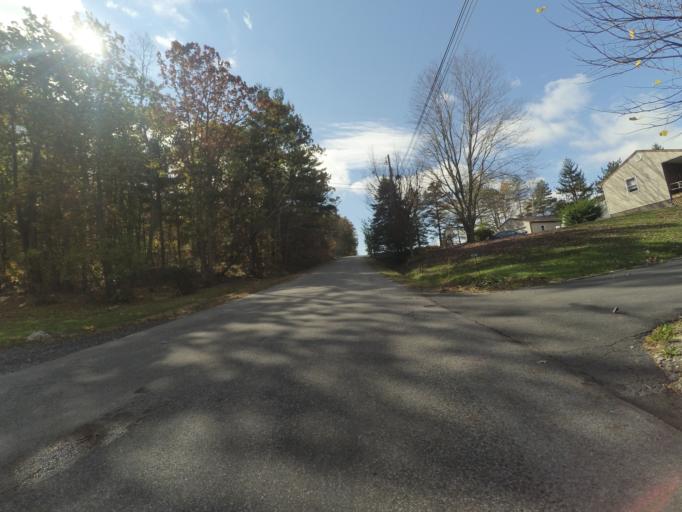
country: US
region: Pennsylvania
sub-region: Centre County
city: Park Forest Village
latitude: 40.8616
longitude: -77.9700
